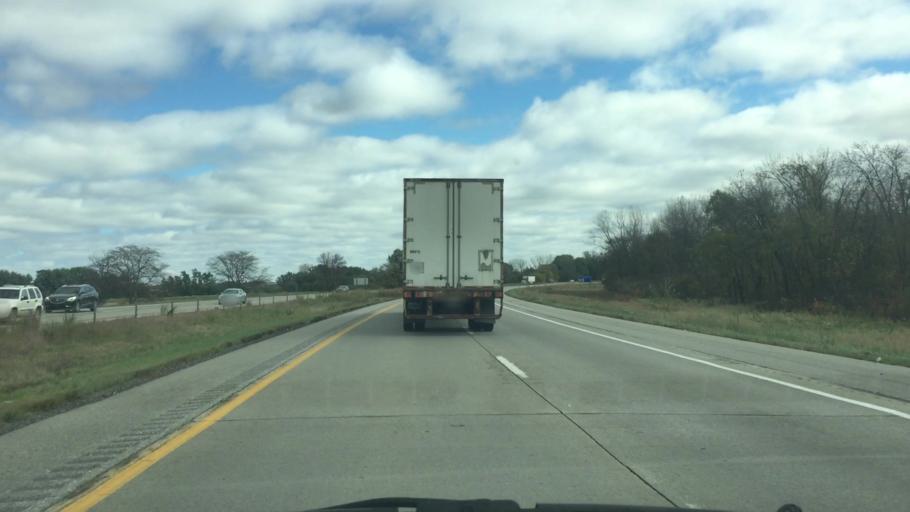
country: US
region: Iowa
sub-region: Jasper County
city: Colfax
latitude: 41.6997
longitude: -93.2081
